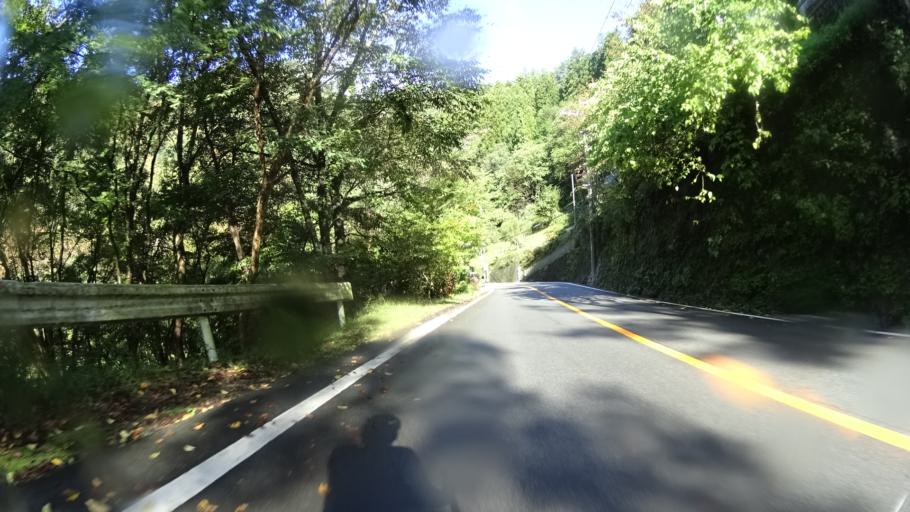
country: JP
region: Yamanashi
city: Otsuki
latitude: 35.7877
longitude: 138.9621
